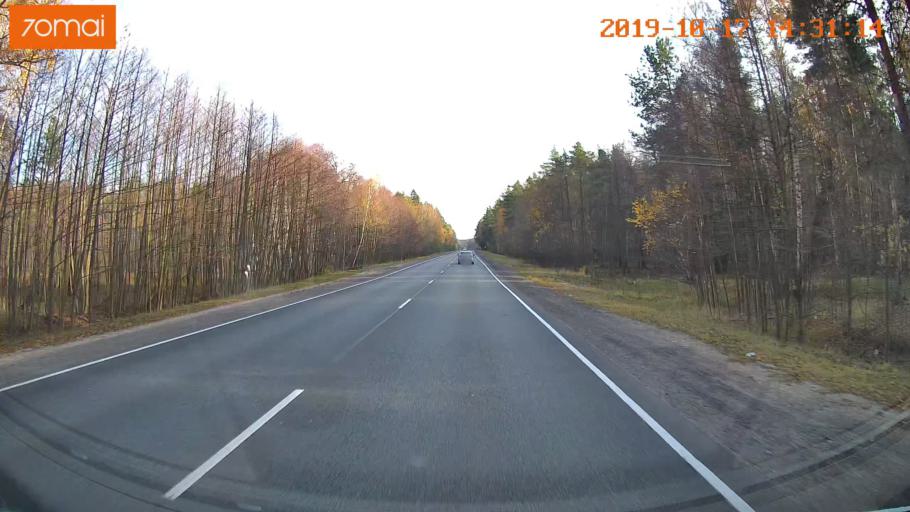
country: RU
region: Rjazan
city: Solotcha
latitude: 54.9386
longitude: 39.9583
